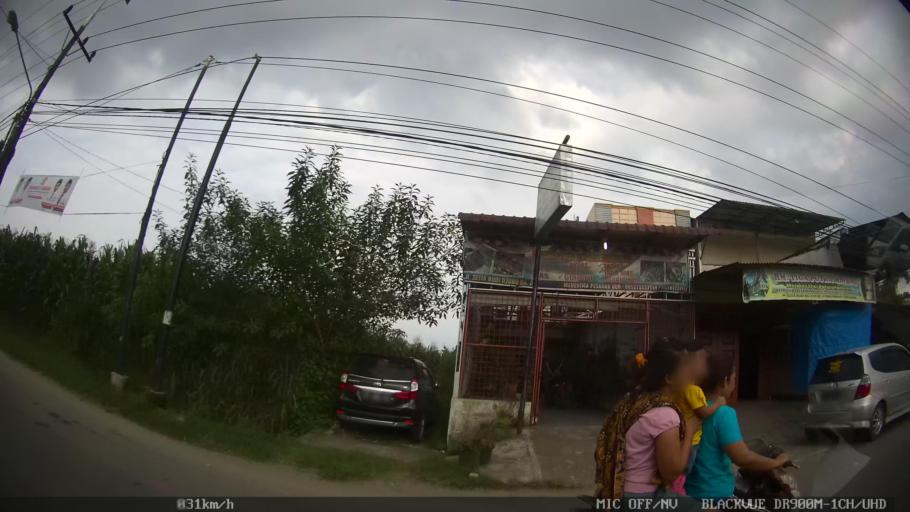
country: ID
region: North Sumatra
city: Sunggal
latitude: 3.5291
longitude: 98.6200
